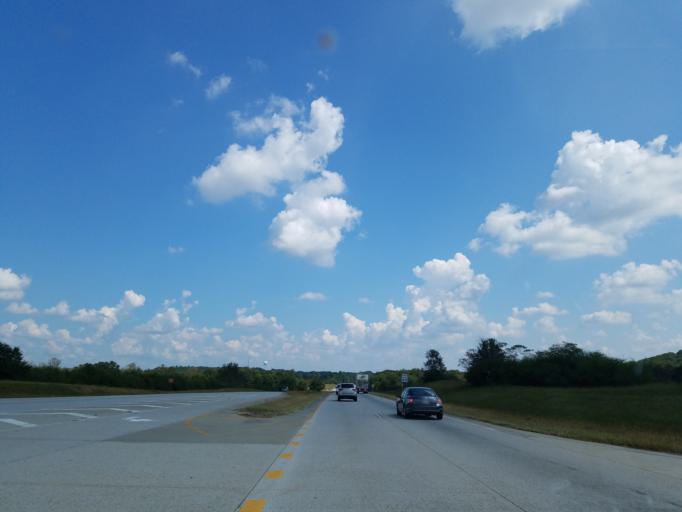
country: US
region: Georgia
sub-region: Barrow County
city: Statham
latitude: 33.9613
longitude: -83.6326
